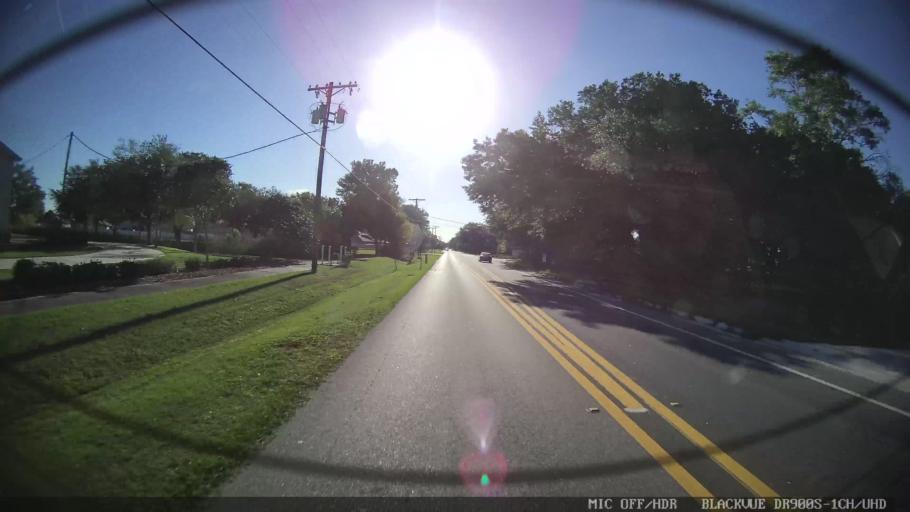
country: US
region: Florida
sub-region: Hillsborough County
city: Sun City Center
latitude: 27.7811
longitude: -82.3375
